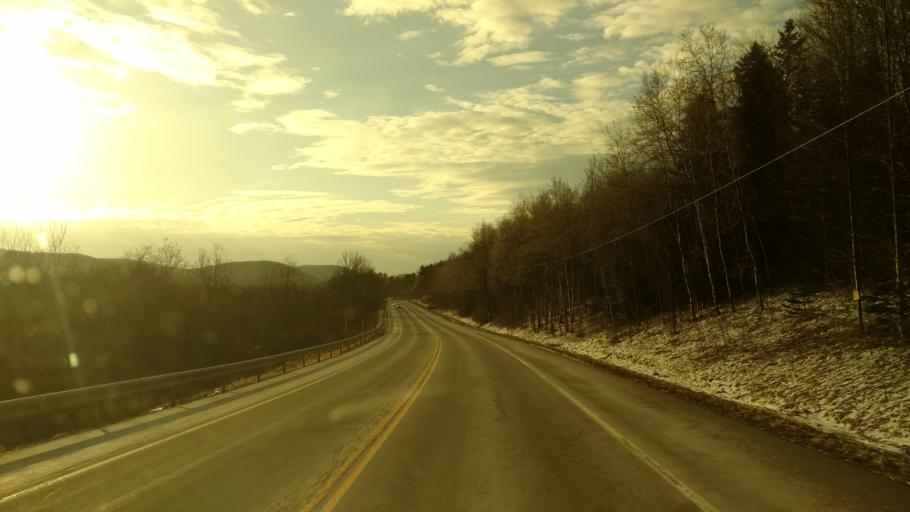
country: US
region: New York
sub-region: Allegany County
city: Wellsville
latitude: 42.0009
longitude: -77.8838
